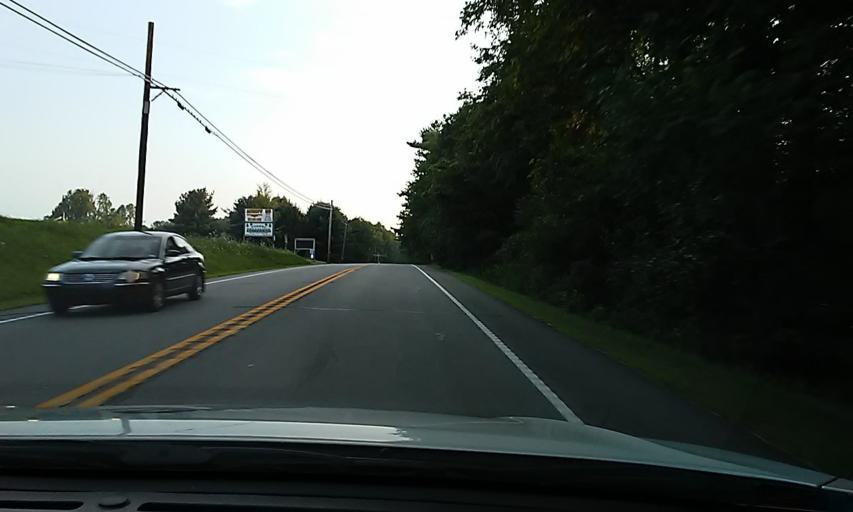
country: US
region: Pennsylvania
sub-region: Forest County
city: Marienville
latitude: 41.4416
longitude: -79.1793
